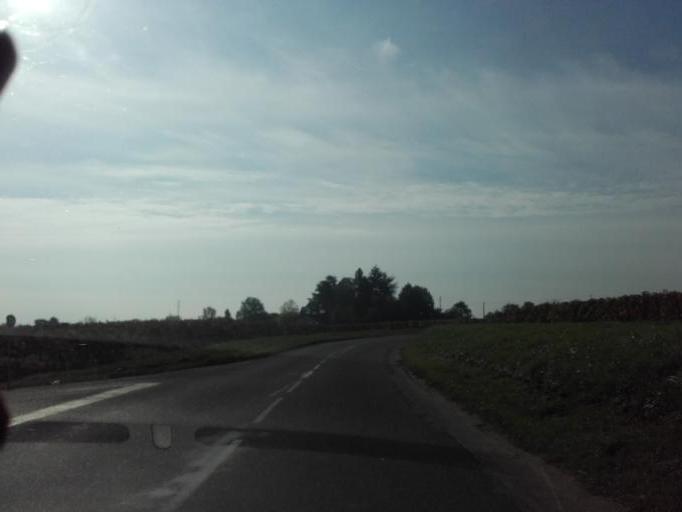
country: FR
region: Bourgogne
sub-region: Departement de Saone-et-Loire
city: Creches-sur-Saone
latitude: 46.2650
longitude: 4.7718
